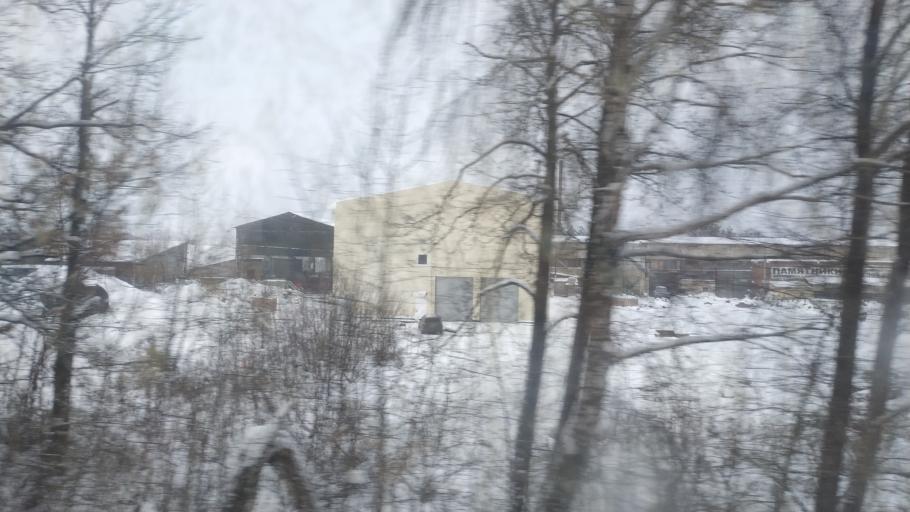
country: RU
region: Moskovskaya
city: Ramenskoye
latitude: 55.5442
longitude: 38.2851
